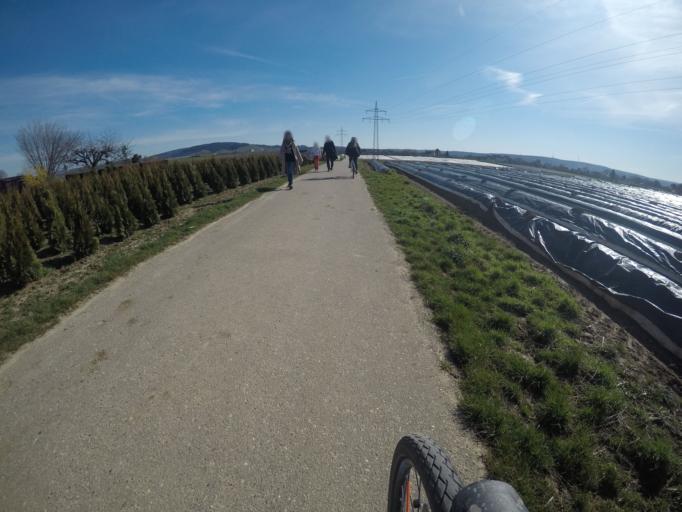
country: DE
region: Baden-Wuerttemberg
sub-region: Regierungsbezirk Stuttgart
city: Stuttgart Muehlhausen
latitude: 48.8272
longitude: 9.2490
